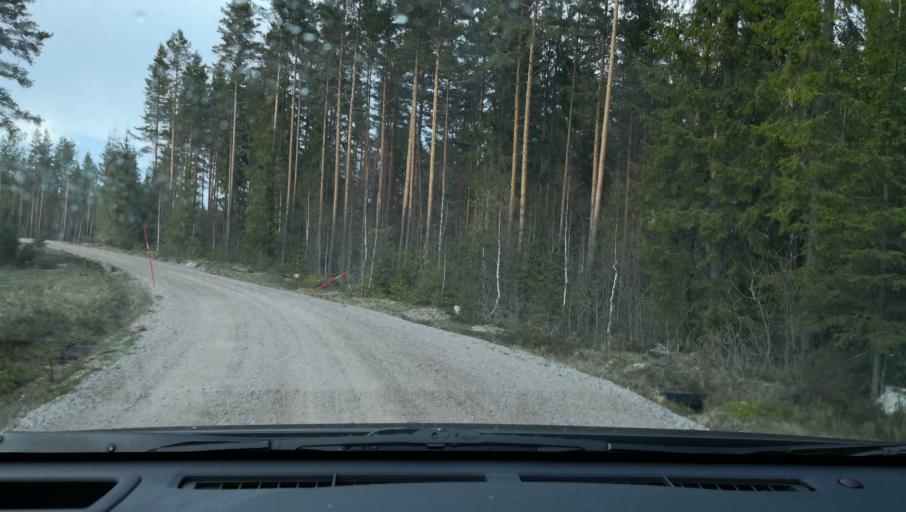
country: SE
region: Dalarna
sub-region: Saters Kommun
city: Saeter
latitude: 60.1713
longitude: 15.7254
